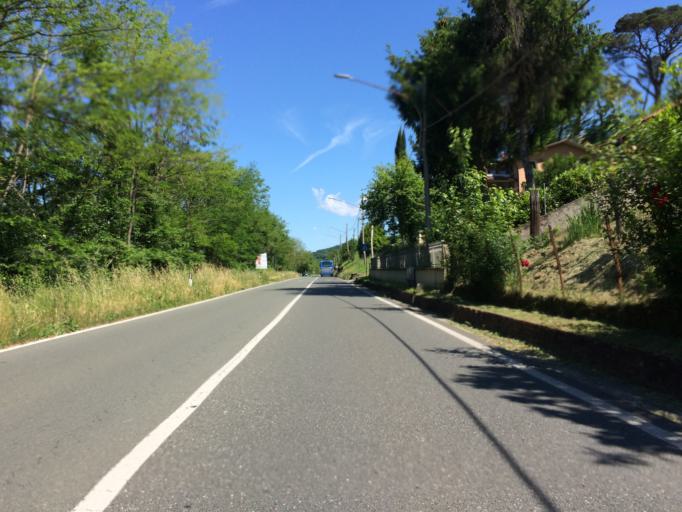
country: IT
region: Tuscany
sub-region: Provincia di Massa-Carrara
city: Terrarossa
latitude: 44.2353
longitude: 9.9602
